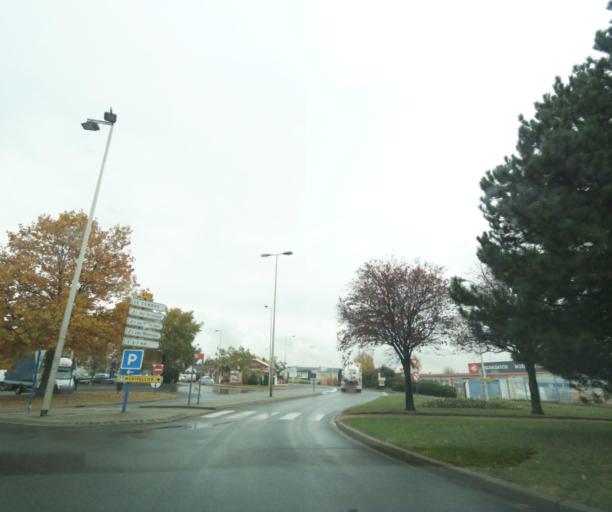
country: FR
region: Auvergne
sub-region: Departement du Puy-de-Dome
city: Perignat-les-Sarlieve
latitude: 45.7548
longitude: 3.1565
